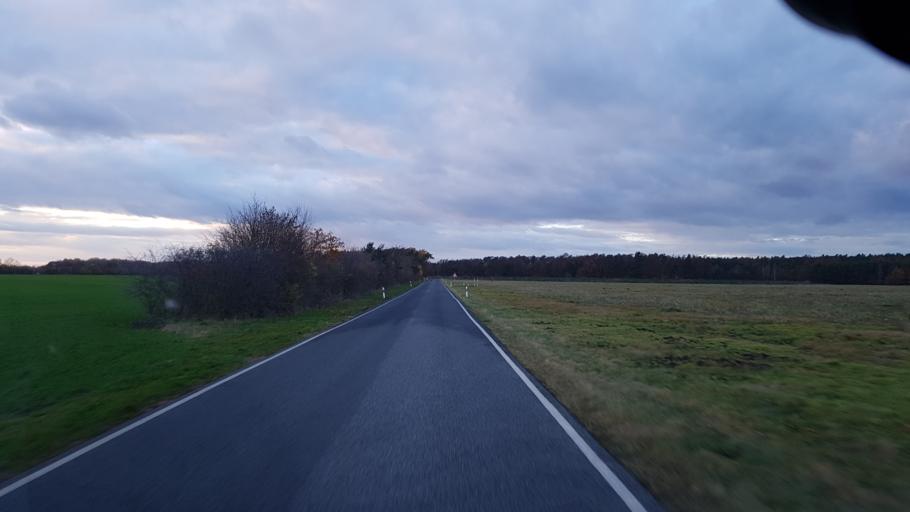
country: DE
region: Brandenburg
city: Tettau
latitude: 51.4225
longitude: 13.7488
